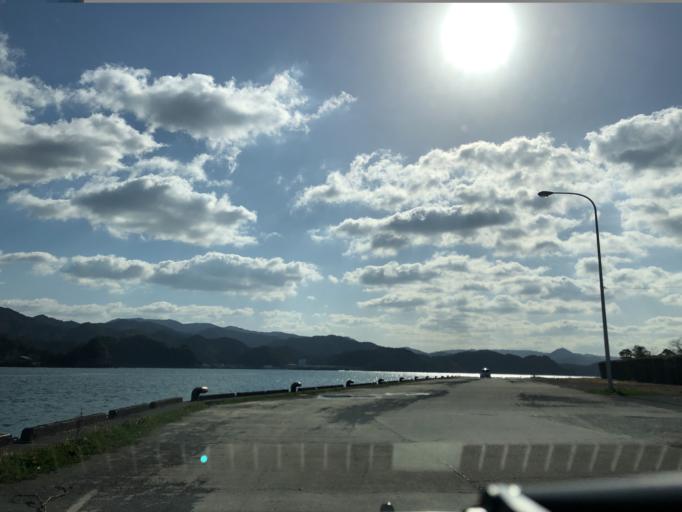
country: JP
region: Kochi
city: Sukumo
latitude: 32.9174
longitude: 132.7043
